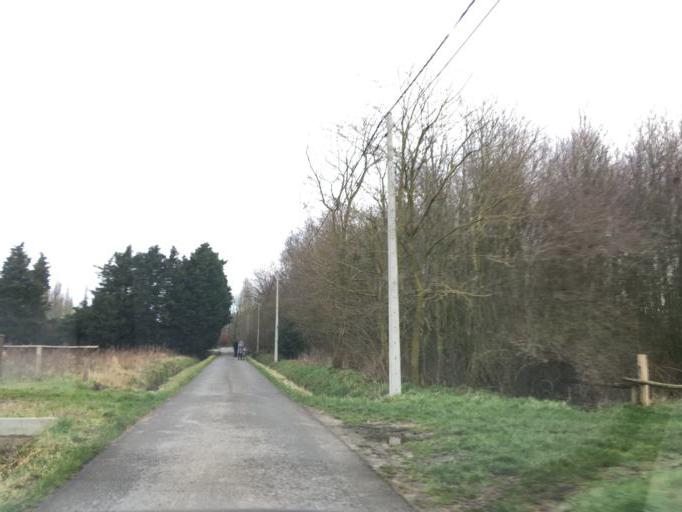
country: BE
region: Flanders
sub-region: Provincie West-Vlaanderen
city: Roeselare
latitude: 50.9164
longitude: 3.1308
